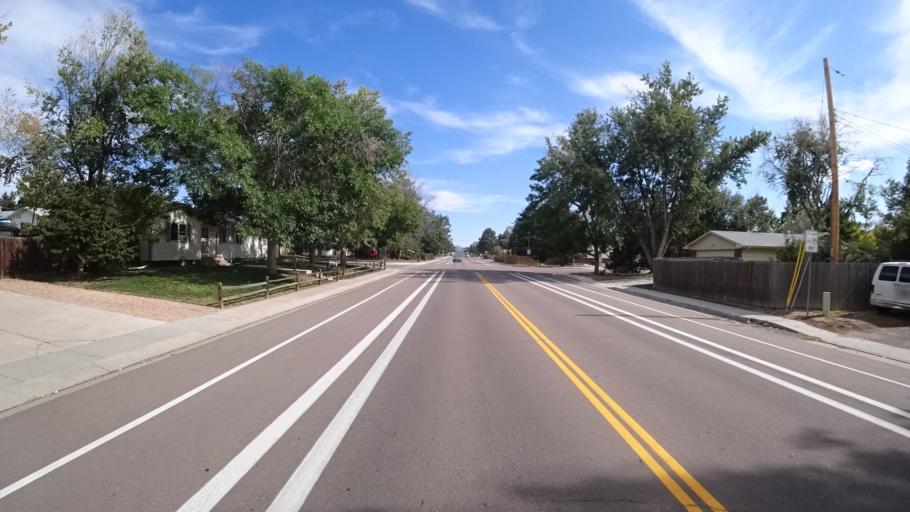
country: US
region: Colorado
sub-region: El Paso County
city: Cimarron Hills
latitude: 38.8945
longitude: -104.7637
